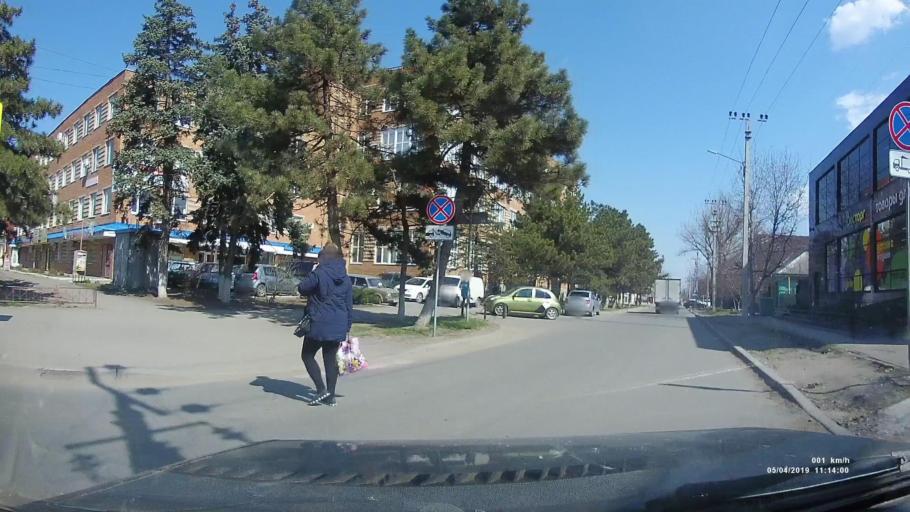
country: RU
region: Rostov
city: Azov
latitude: 47.1039
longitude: 39.4290
